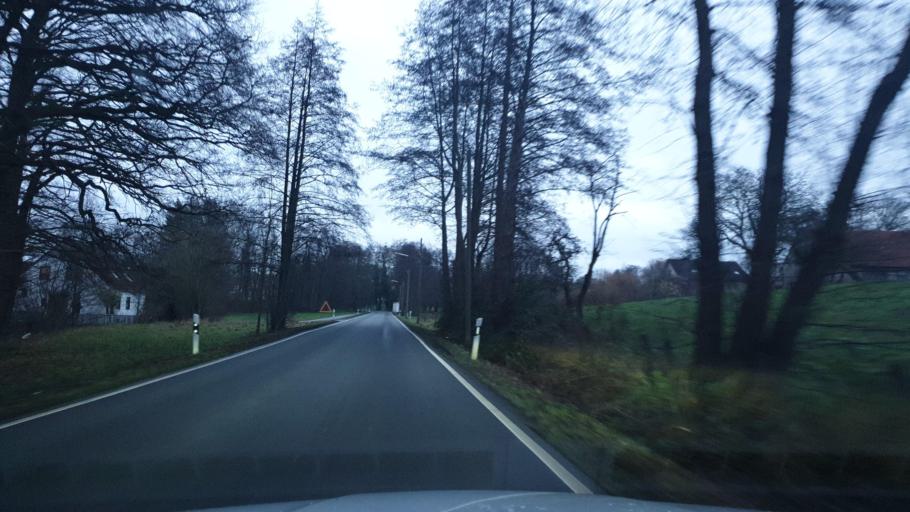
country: DE
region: North Rhine-Westphalia
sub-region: Regierungsbezirk Detmold
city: Vlotho
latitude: 52.1671
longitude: 8.8256
